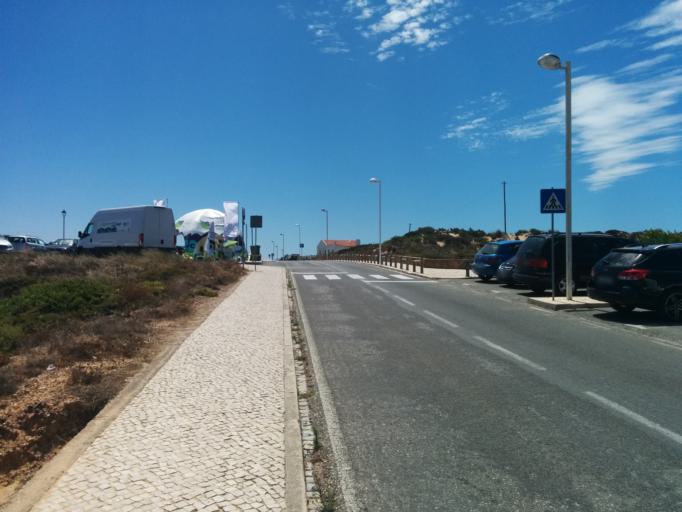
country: PT
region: Beja
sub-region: Odemira
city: Vila Nova de Milfontes
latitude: 37.7208
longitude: -8.7891
